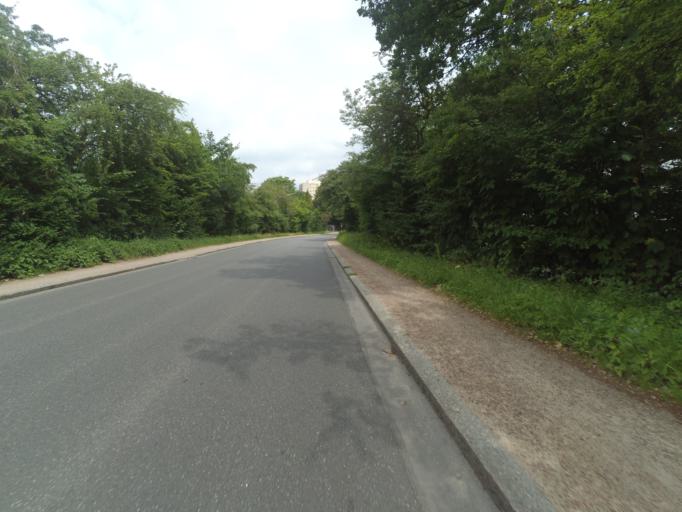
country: DE
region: Schleswig-Holstein
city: Barsbuettel
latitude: 53.5683
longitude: 10.1341
